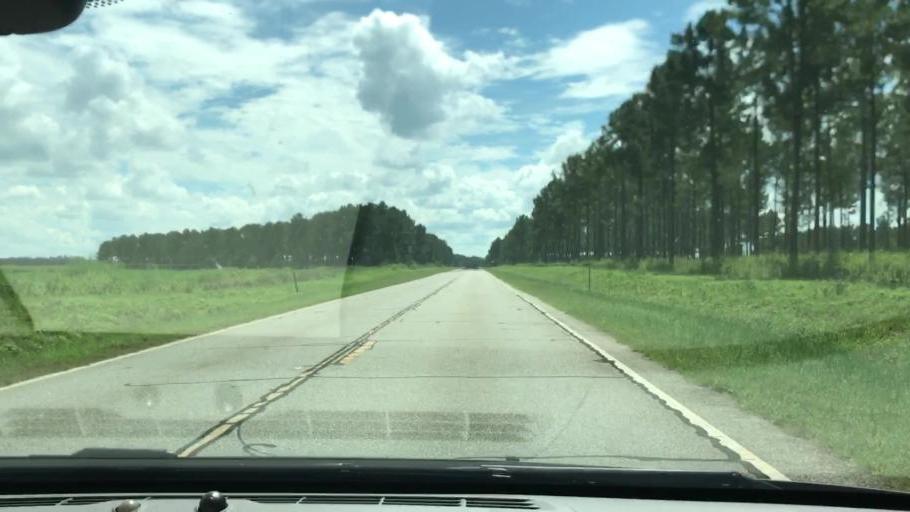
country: US
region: Georgia
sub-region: Quitman County
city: Georgetown
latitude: 32.0646
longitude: -85.0362
